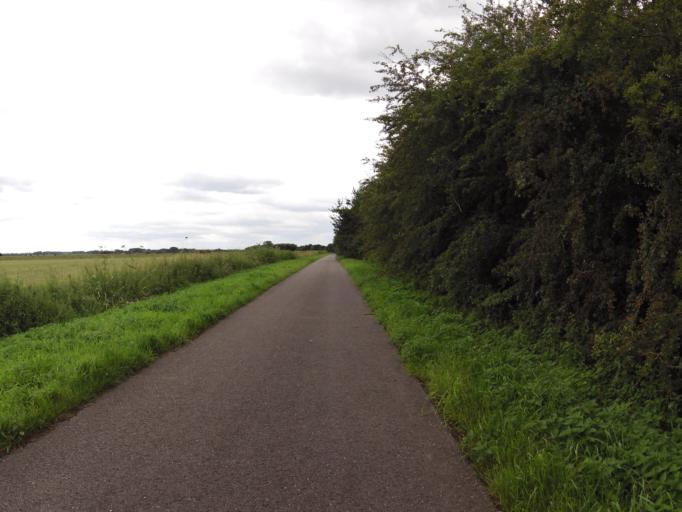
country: NL
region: North Brabant
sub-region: Gemeente Landerd
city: Reek
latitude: 51.7738
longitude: 5.6793
